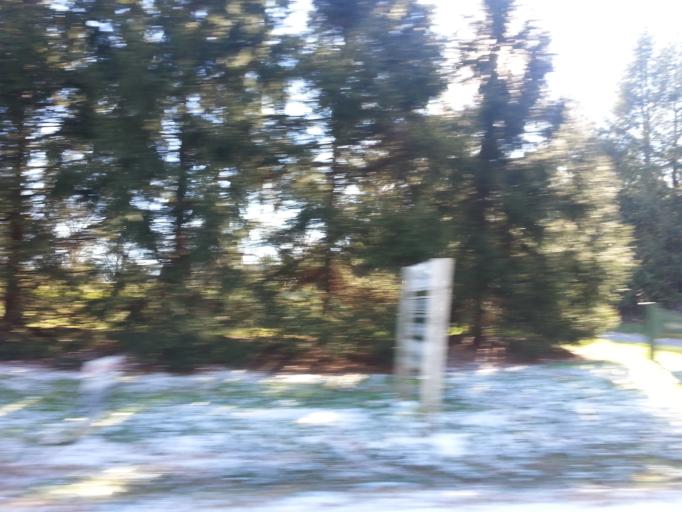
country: US
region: Tennessee
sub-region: Knox County
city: Knoxville
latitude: 35.9225
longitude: -84.0003
